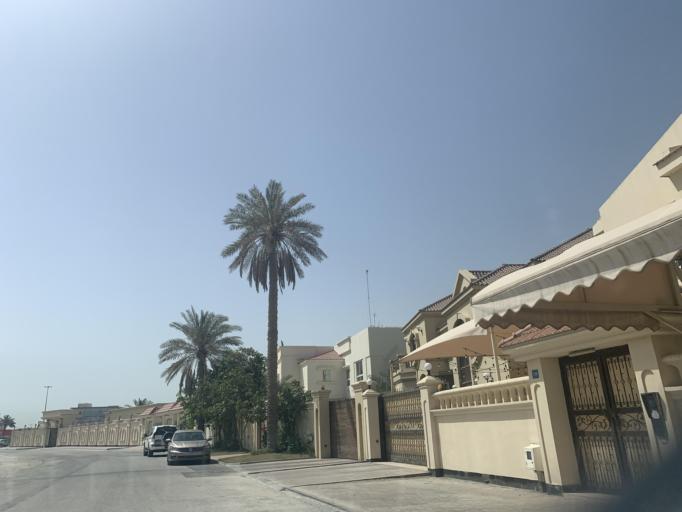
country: BH
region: Manama
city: Jidd Hafs
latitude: 26.2000
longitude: 50.5548
